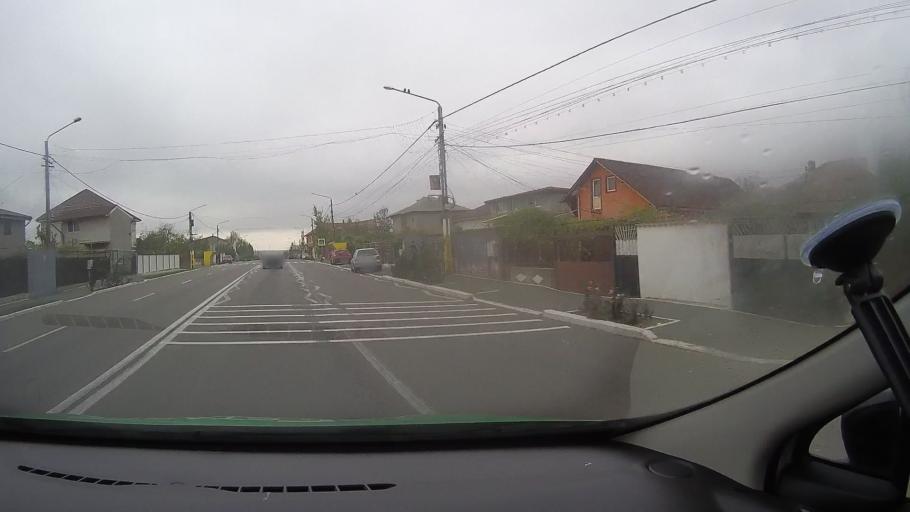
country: RO
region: Constanta
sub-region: Comuna Valu lui Traian
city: Valu lui Traian
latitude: 44.1675
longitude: 28.4531
